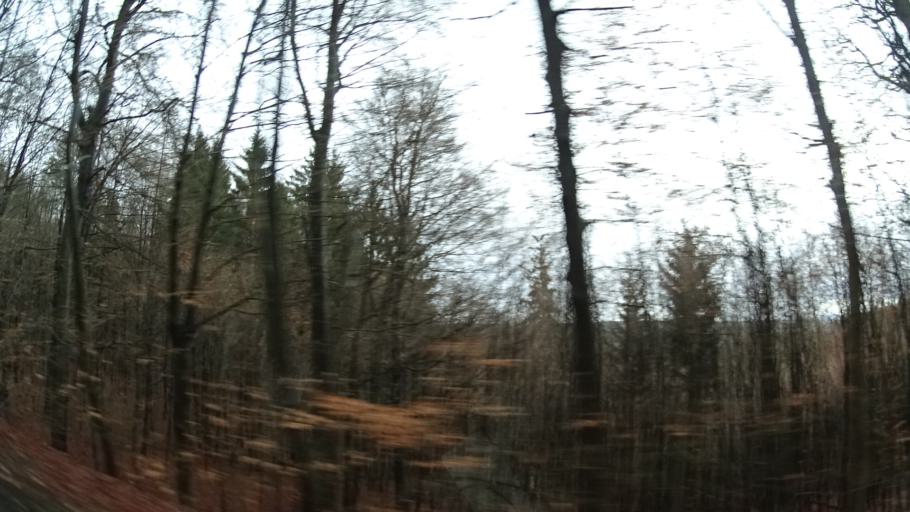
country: DE
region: Hesse
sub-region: Regierungsbezirk Giessen
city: Lauterbach
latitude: 50.6651
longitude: 9.4301
